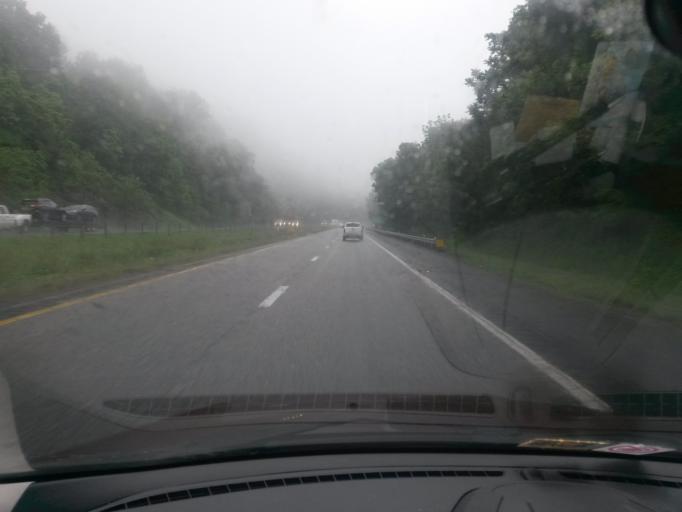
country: US
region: Virginia
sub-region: City of Waynesboro
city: Waynesboro
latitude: 38.0363
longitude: -78.8429
